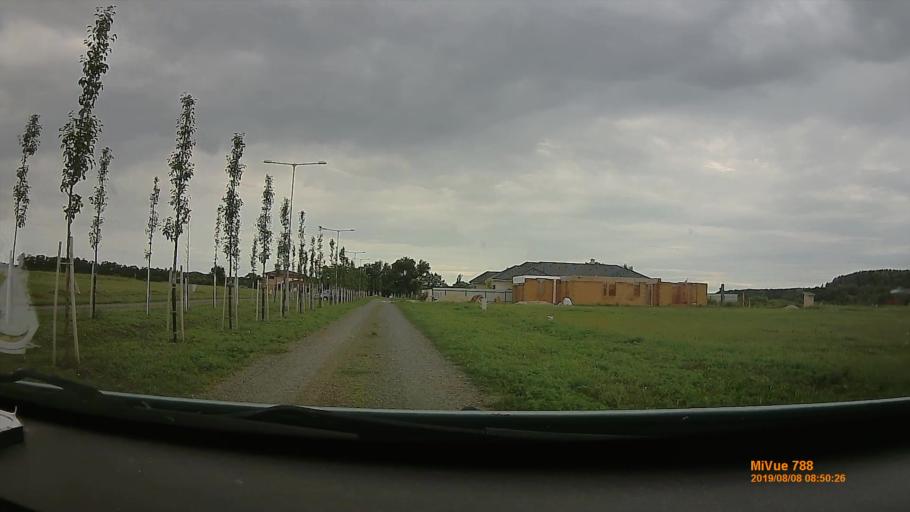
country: HU
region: Hajdu-Bihar
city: Debrecen
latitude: 47.6007
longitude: 21.6438
